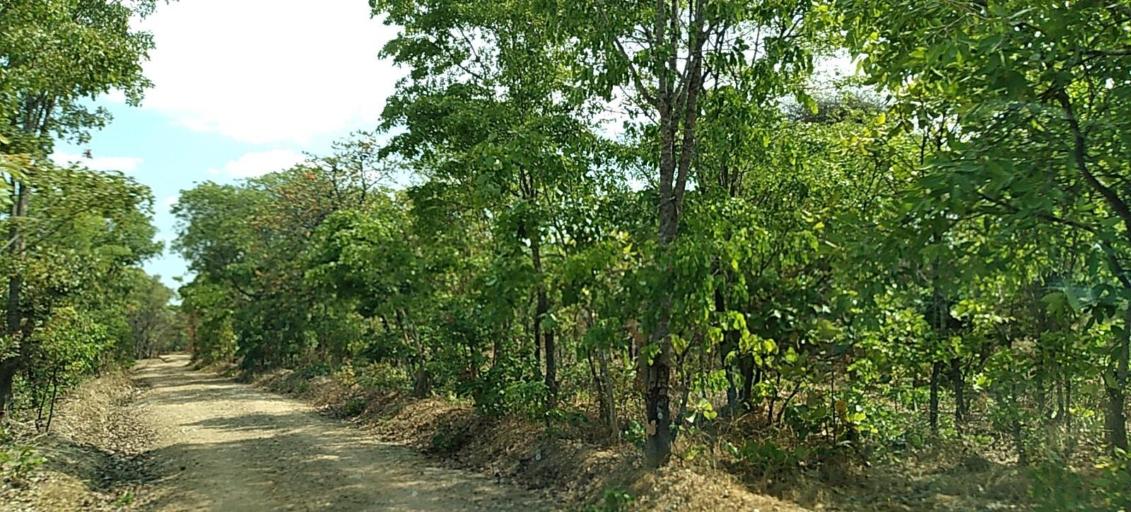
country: ZM
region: Copperbelt
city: Chililabombwe
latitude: -12.3223
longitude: 27.7879
